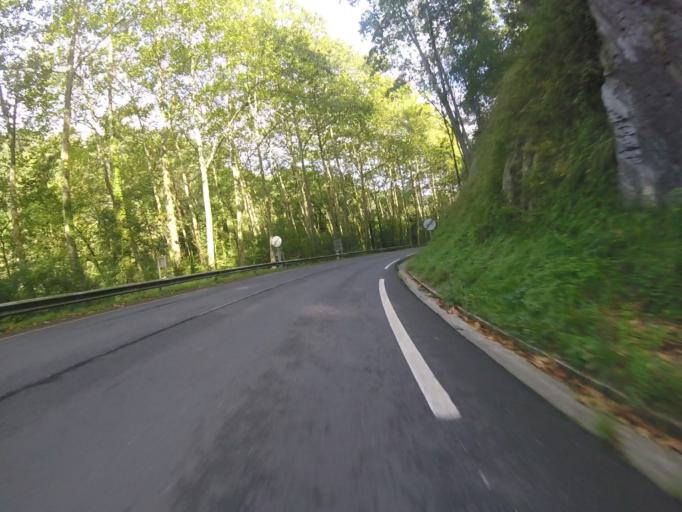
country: ES
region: Basque Country
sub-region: Provincia de Guipuzcoa
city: Orendain
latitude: 43.0767
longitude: -2.0876
